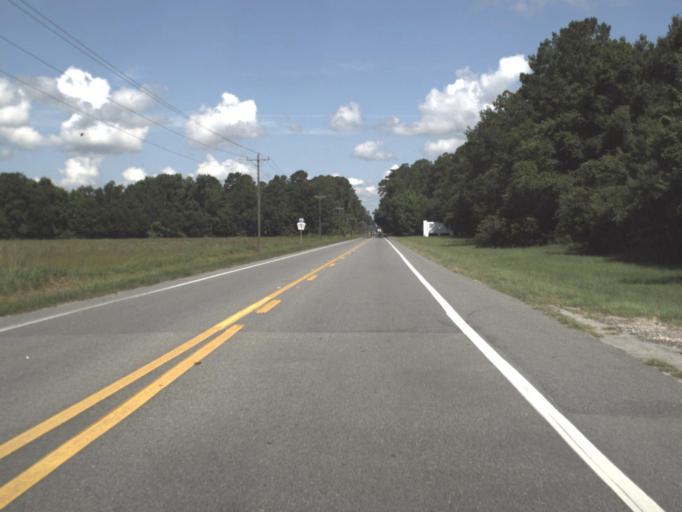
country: US
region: Florida
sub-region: Putnam County
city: Palatka
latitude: 29.6762
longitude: -81.7160
